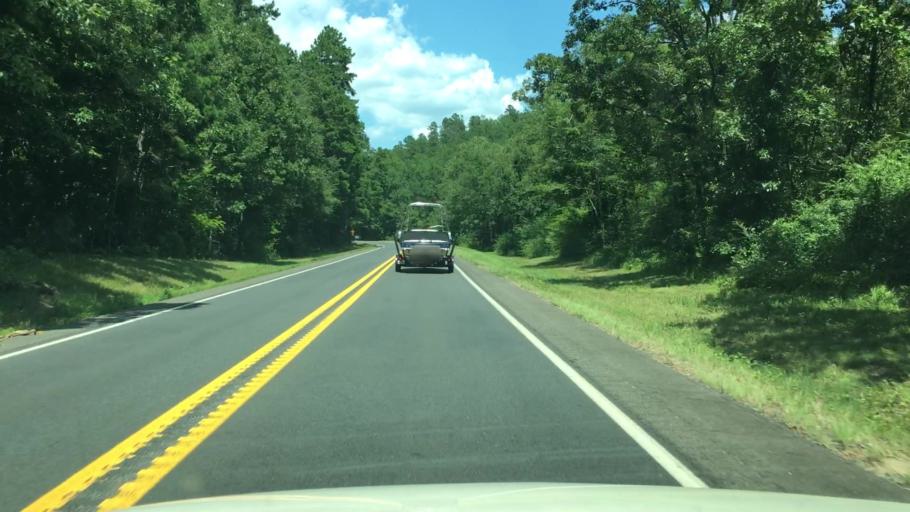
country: US
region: Arkansas
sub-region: Garland County
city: Lake Hamilton
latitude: 34.3557
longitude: -93.1807
